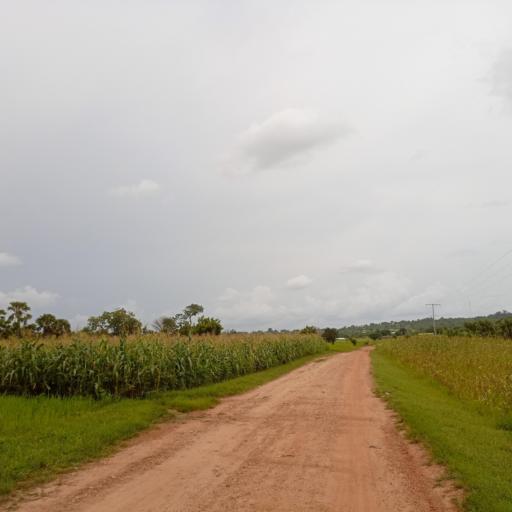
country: TG
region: Savanes
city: Dapaong
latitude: 10.8073
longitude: 0.0279
